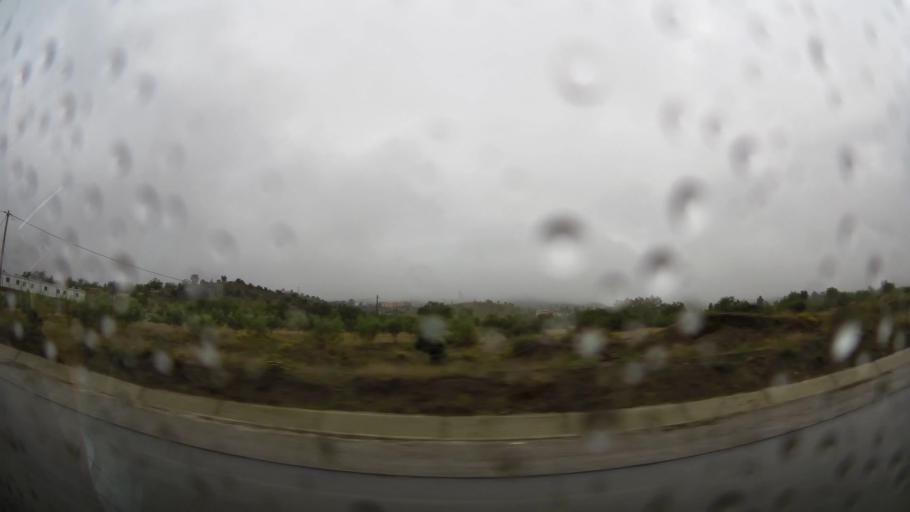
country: MA
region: Oriental
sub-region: Nador
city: Midar
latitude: 34.8651
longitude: -3.7244
